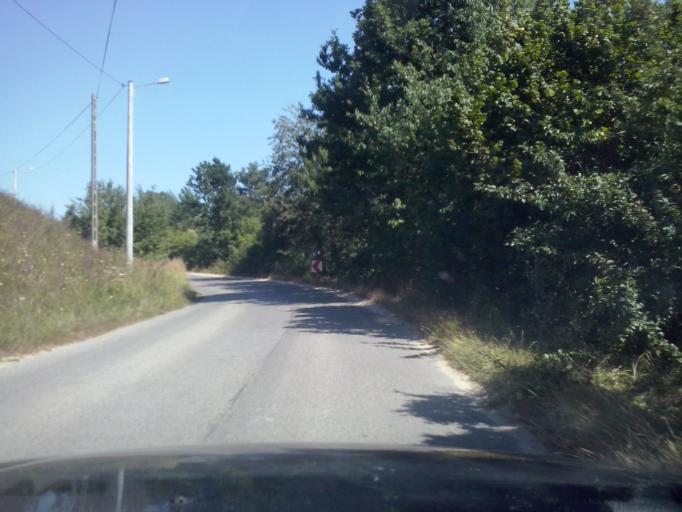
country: PL
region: Swietokrzyskie
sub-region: Powiat kielecki
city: Bieliny
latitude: 50.8068
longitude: 20.9558
